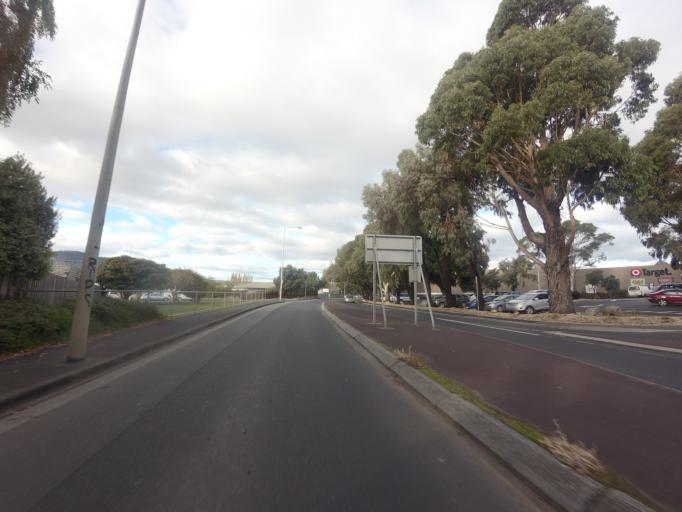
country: AU
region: Tasmania
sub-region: Glenorchy
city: Glenorchy
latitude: -42.8312
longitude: 147.2718
